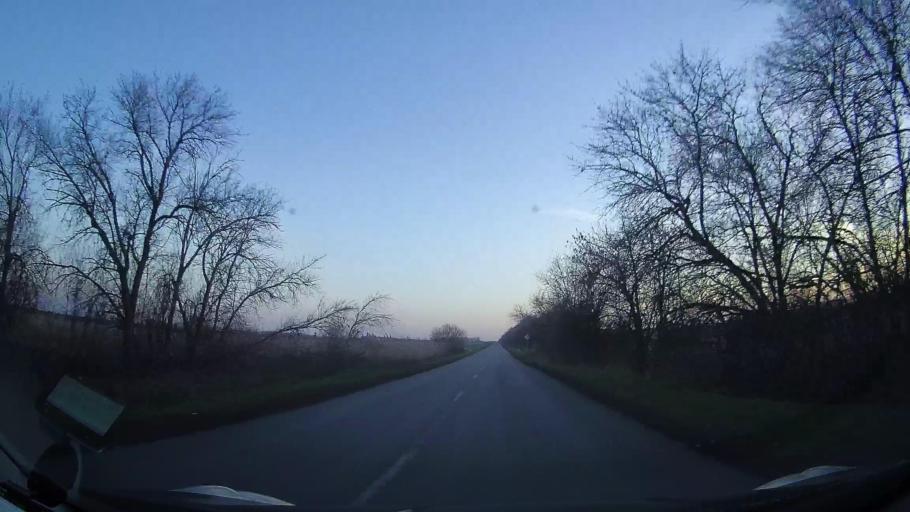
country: RU
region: Rostov
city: Zernograd
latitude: 47.0427
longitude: 40.3916
